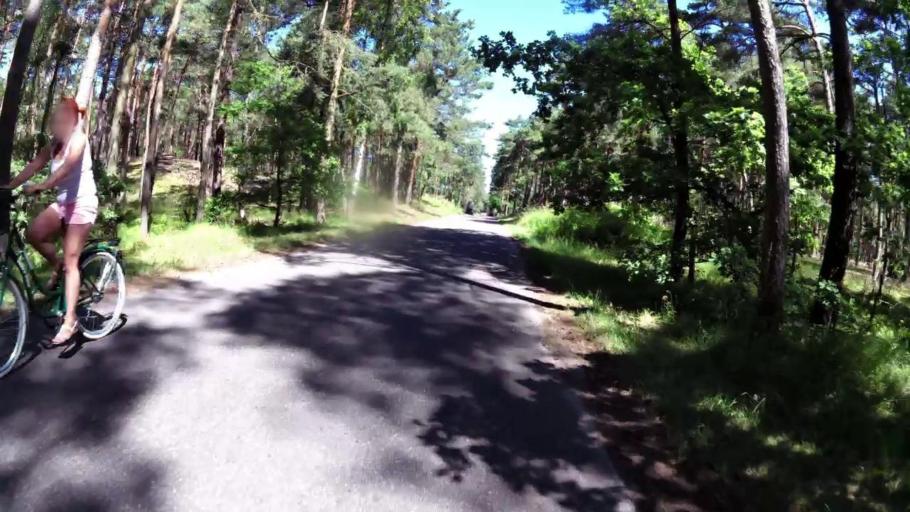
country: PL
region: West Pomeranian Voivodeship
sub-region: Powiat gryficki
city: Pobierowo
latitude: 54.0522
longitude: 14.9197
